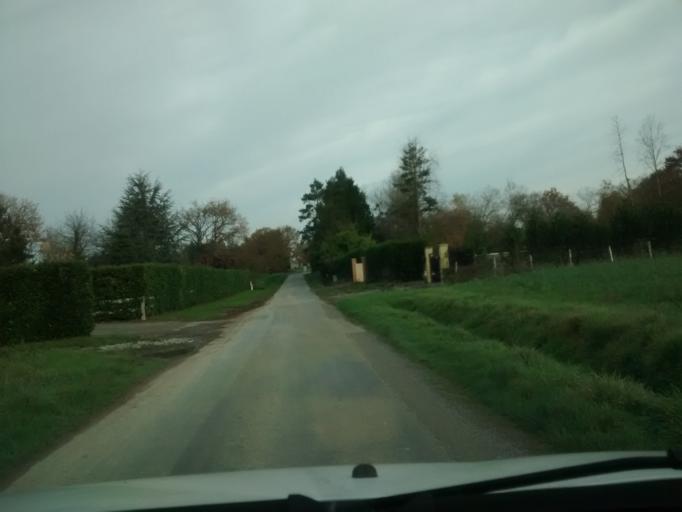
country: FR
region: Brittany
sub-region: Departement d'Ille-et-Vilaine
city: Noyal-sur-Vilaine
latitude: 48.0888
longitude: -1.5505
